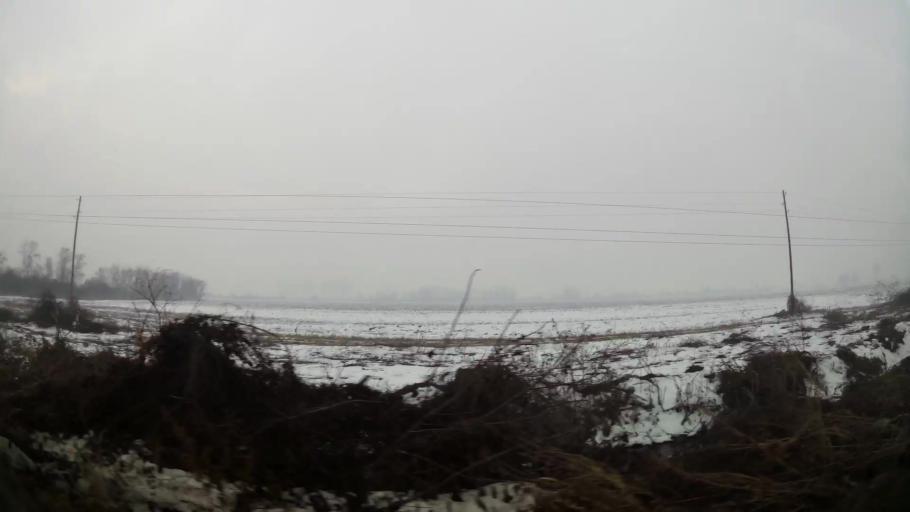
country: MK
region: Ilinden
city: Idrizovo
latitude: 41.9492
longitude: 21.5889
